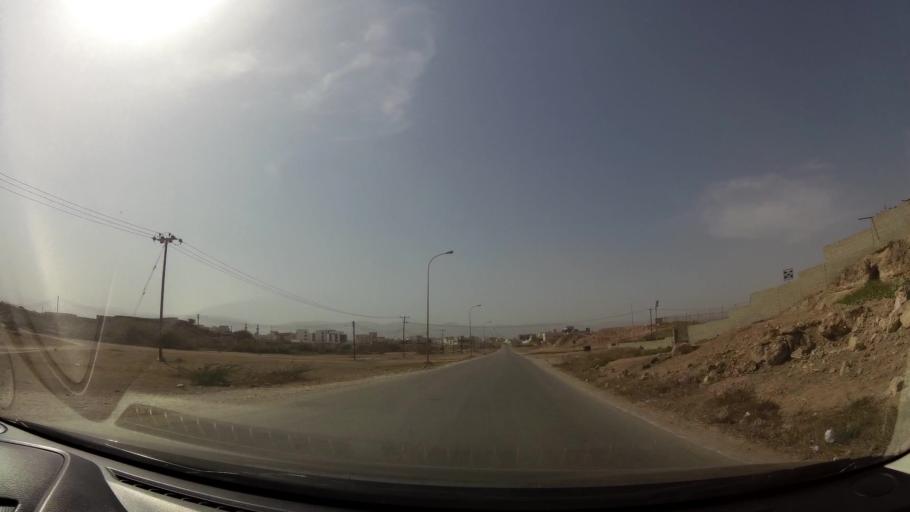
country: OM
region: Zufar
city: Salalah
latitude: 16.9952
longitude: 54.0195
